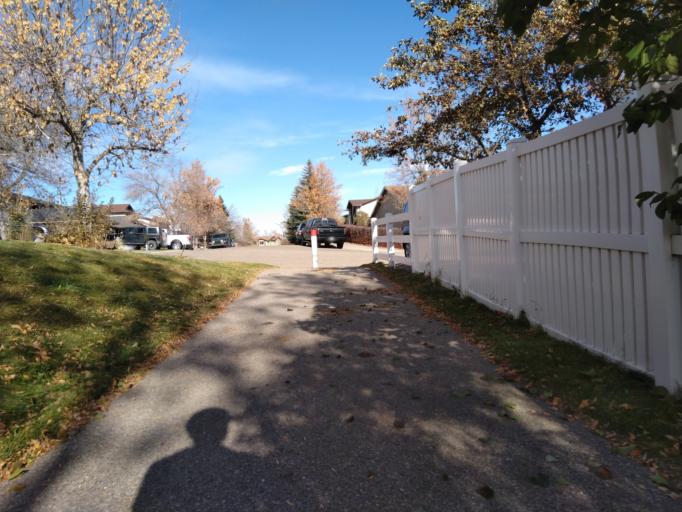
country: CA
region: Alberta
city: Calgary
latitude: 51.1253
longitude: -114.0886
